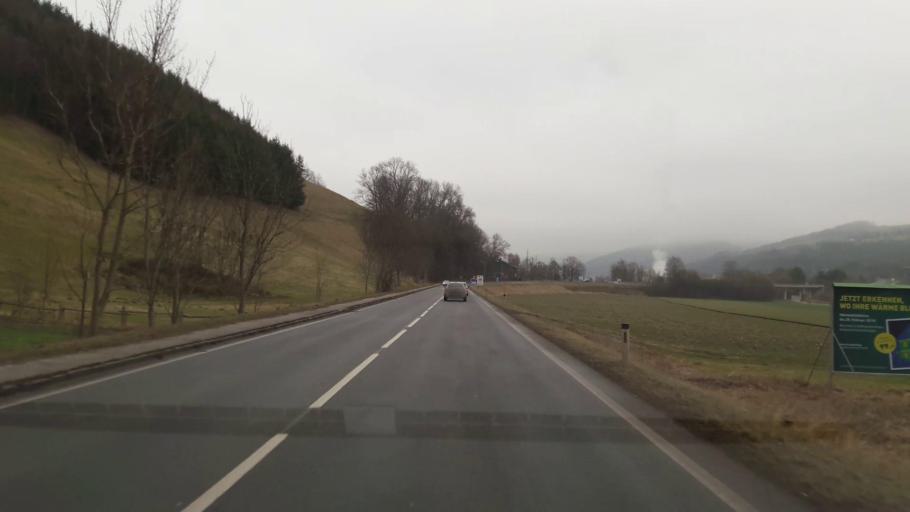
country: AT
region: Lower Austria
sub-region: Politischer Bezirk Neunkirchen
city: Grimmenstein
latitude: 47.6037
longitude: 16.1184
